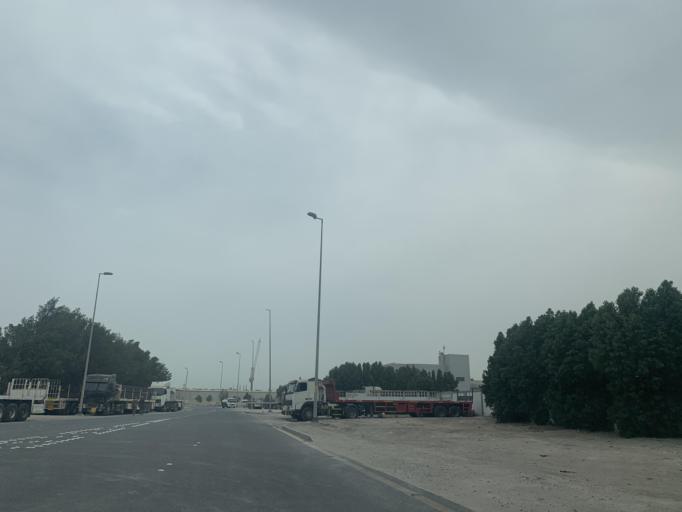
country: BH
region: Muharraq
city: Al Hadd
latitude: 26.2114
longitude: 50.6673
